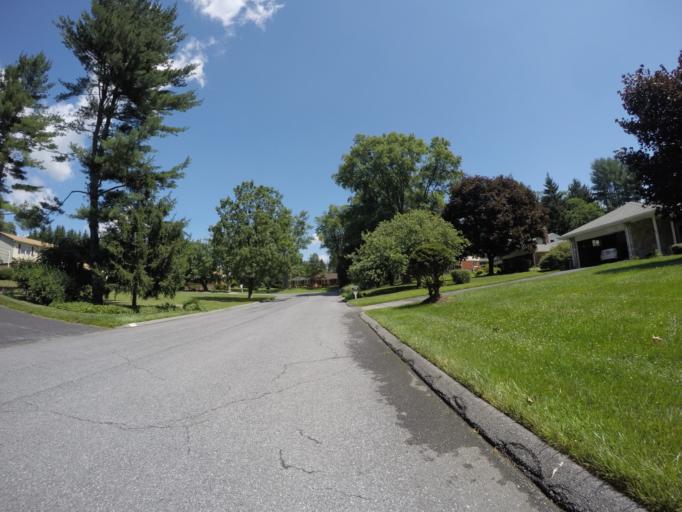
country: US
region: Maryland
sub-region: Howard County
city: Columbia
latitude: 39.2753
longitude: -76.8580
